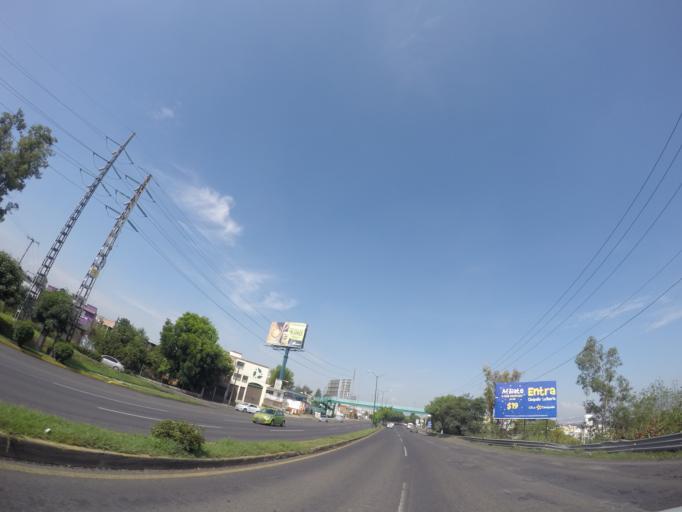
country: MX
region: Michoacan
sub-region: Morelia
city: Morelos
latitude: 19.6771
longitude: -101.2207
